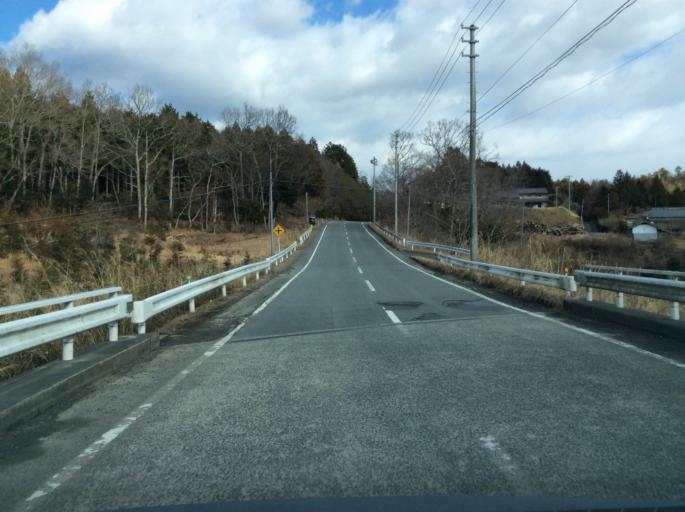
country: JP
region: Fukushima
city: Iwaki
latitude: 37.1647
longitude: 140.9469
